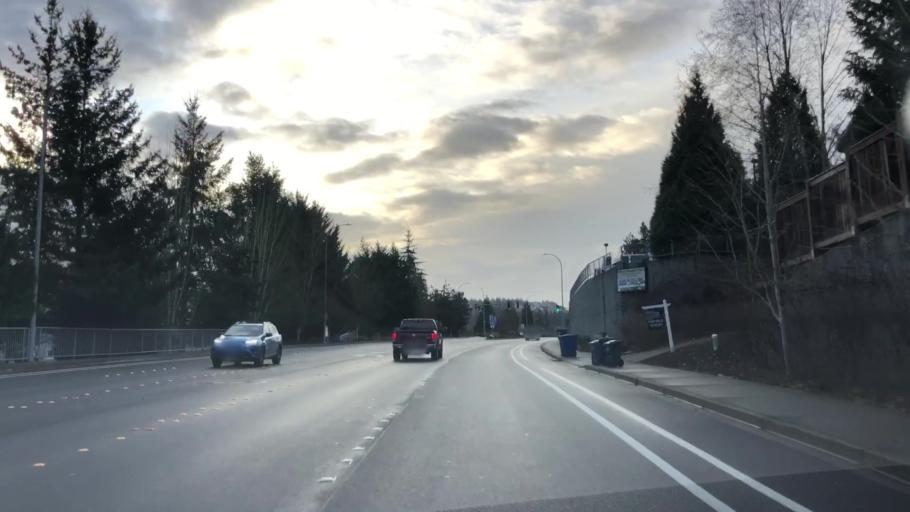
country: US
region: Washington
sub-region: King County
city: Newport
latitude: 47.5931
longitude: -122.1647
